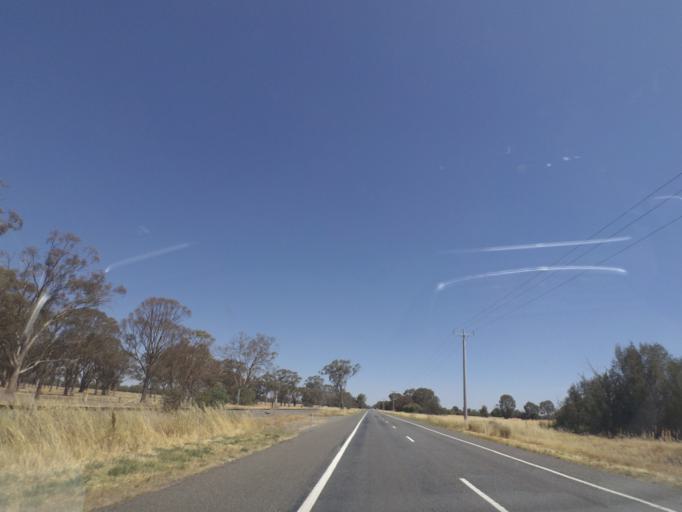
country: AU
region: Victoria
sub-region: Greater Shepparton
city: Shepparton
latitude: -36.2100
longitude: 145.4319
